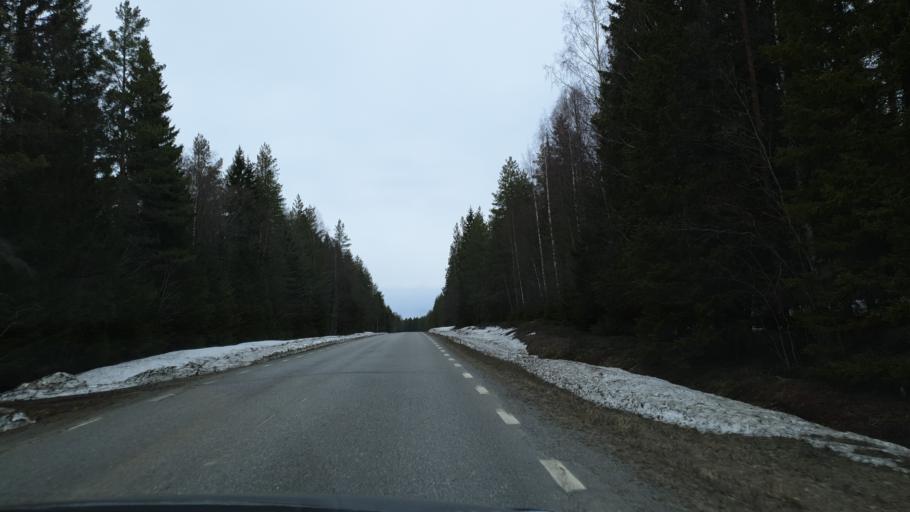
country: SE
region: Vaesterbotten
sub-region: Robertsfors Kommun
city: Robertsfors
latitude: 64.4064
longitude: 20.8764
